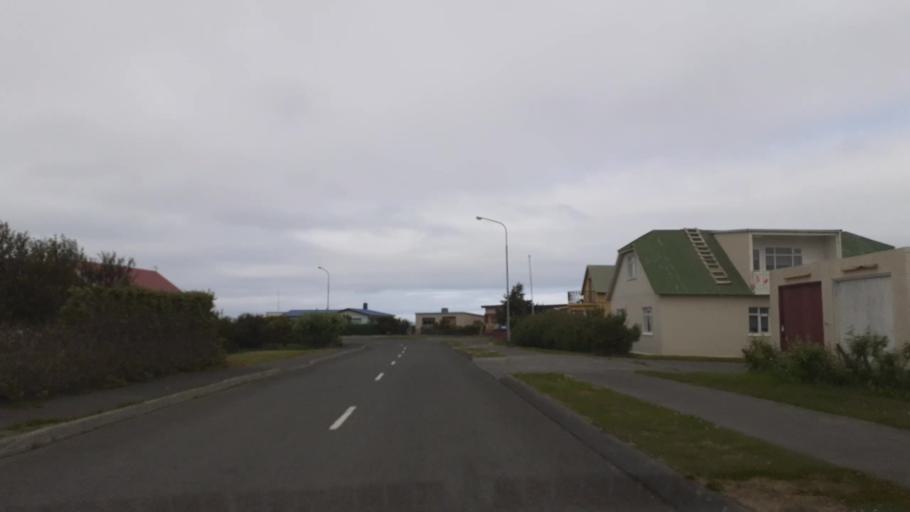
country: IS
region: Northwest
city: Saudarkrokur
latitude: 65.6583
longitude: -20.3018
